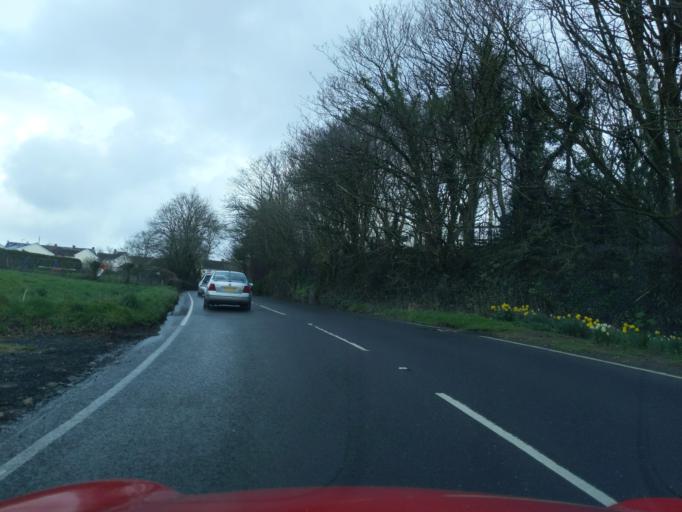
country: GB
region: England
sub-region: Devon
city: Great Torrington
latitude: 50.9508
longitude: -4.1367
